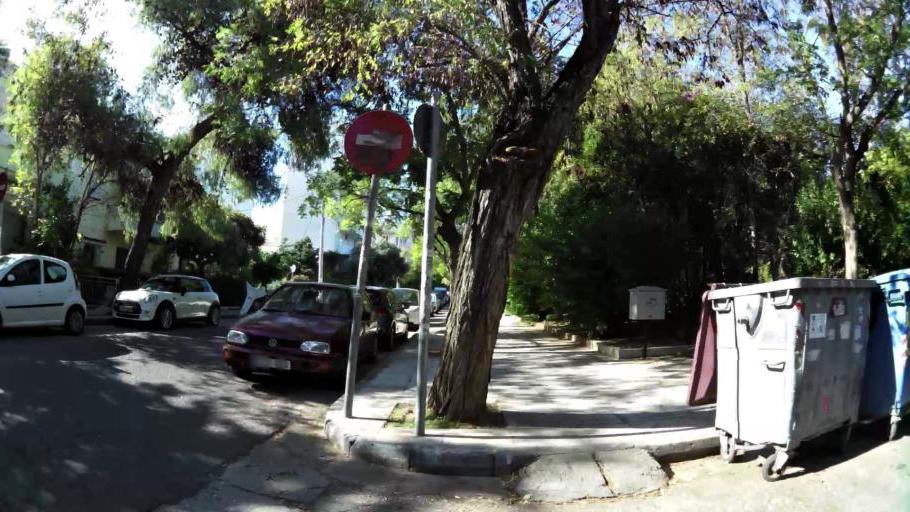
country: GR
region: Attica
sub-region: Nomarchia Athinas
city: Neo Psychiko
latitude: 37.9996
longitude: 23.7753
